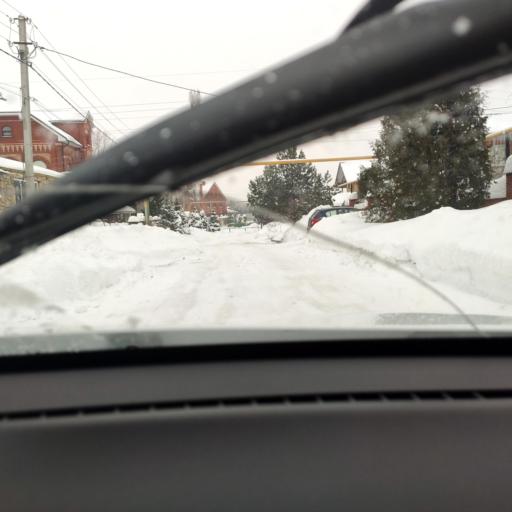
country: RU
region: Tatarstan
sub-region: Gorod Kazan'
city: Kazan
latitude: 55.7275
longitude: 49.1638
